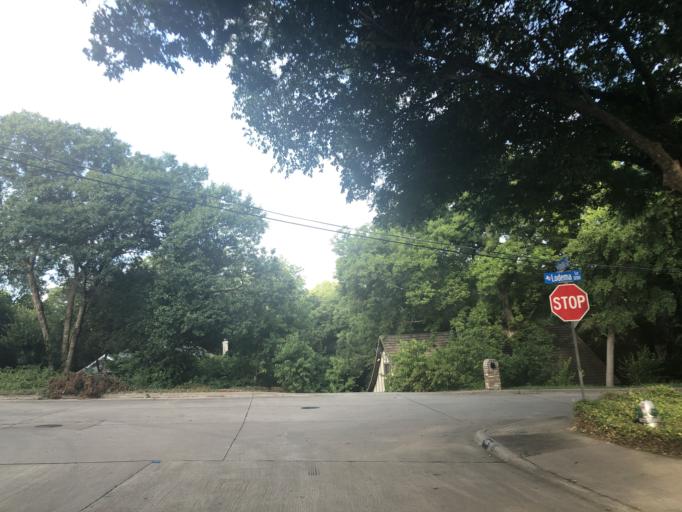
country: US
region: Texas
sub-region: Dallas County
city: Duncanville
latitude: 32.6718
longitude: -96.9129
